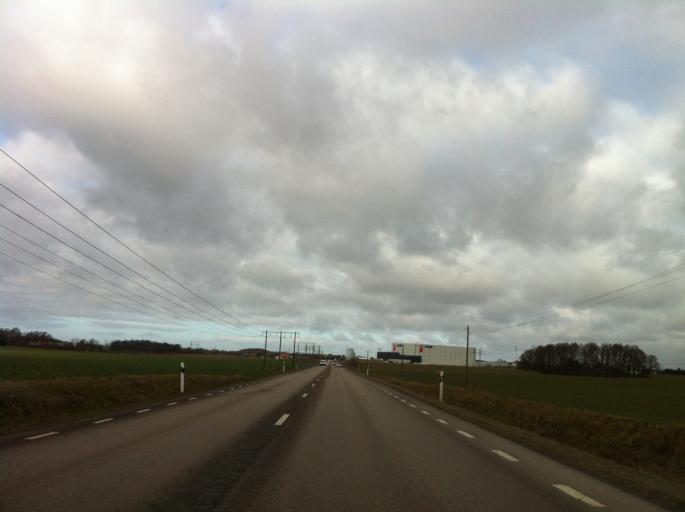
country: SE
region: Skane
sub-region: Bjuvs Kommun
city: Billesholm
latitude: 56.0378
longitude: 12.9697
